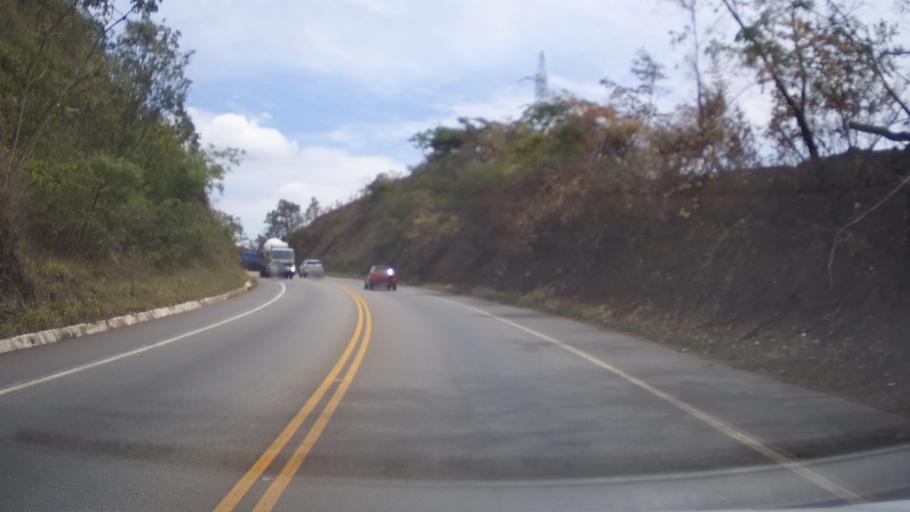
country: BR
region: Minas Gerais
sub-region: Nova Lima
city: Nova Lima
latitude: -19.9926
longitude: -43.8576
